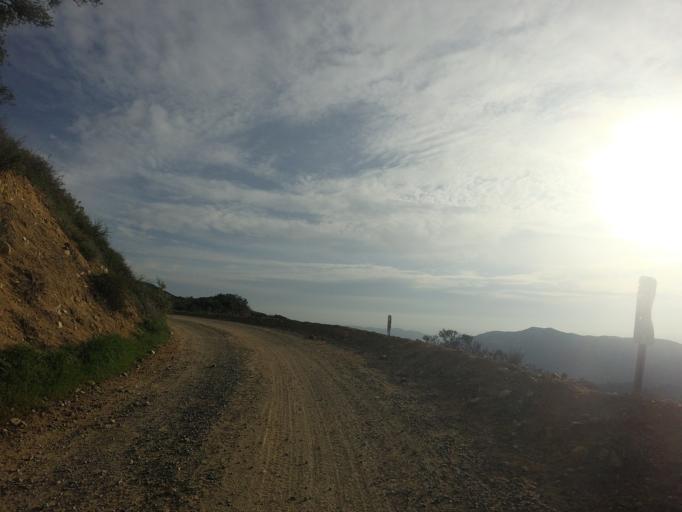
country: US
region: California
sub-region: Riverside County
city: Corona
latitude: 33.8247
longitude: -117.6386
